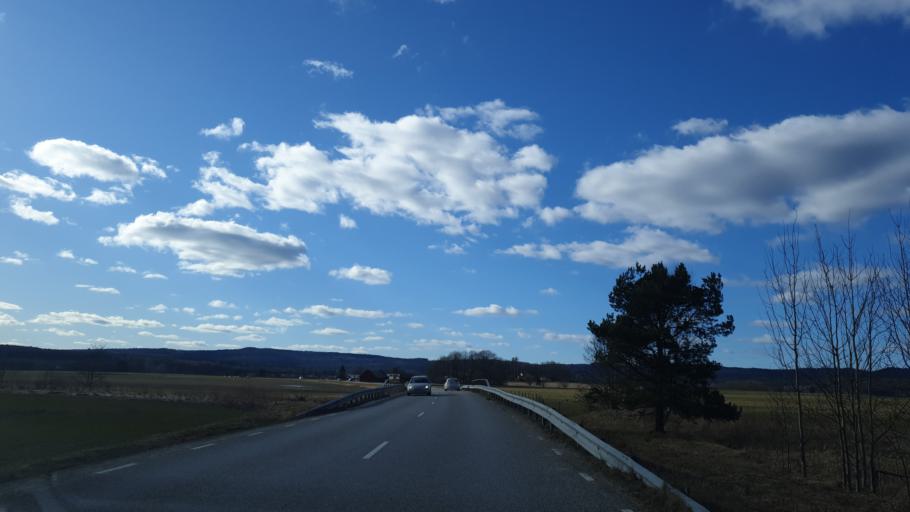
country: SE
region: OErebro
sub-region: Orebro Kommun
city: Garphyttan
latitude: 59.3409
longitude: 15.0542
